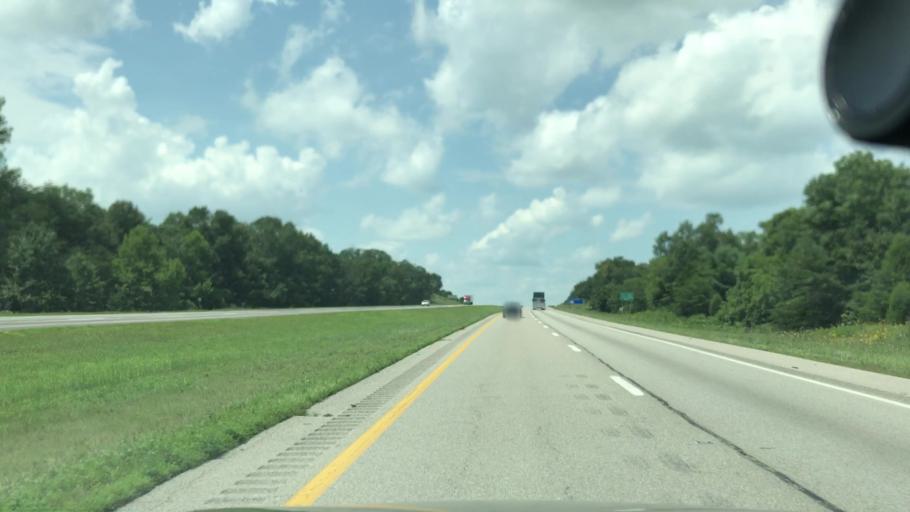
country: US
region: Ohio
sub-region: Gallia County
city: Gallipolis
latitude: 38.8712
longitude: -82.2791
